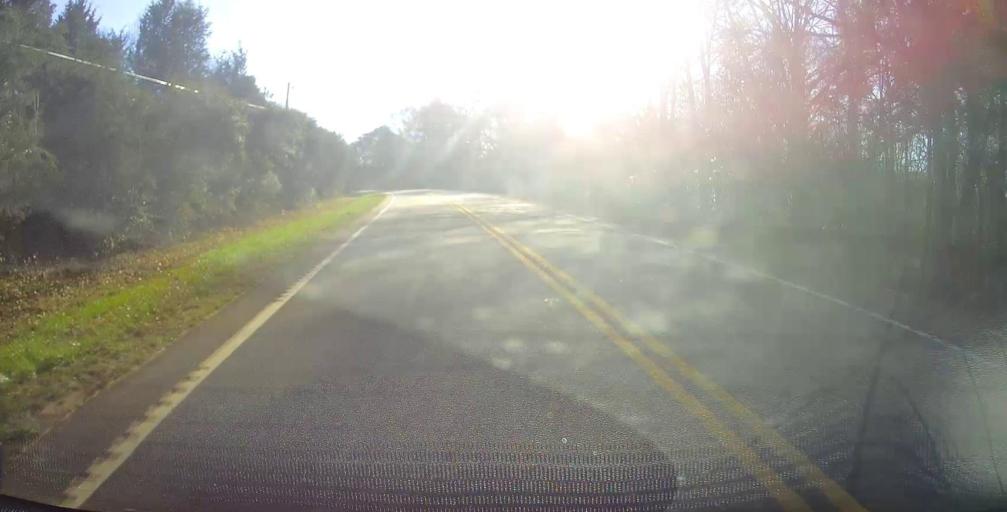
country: US
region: Georgia
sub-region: Meriwether County
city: Manchester
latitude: 32.9108
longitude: -84.6747
